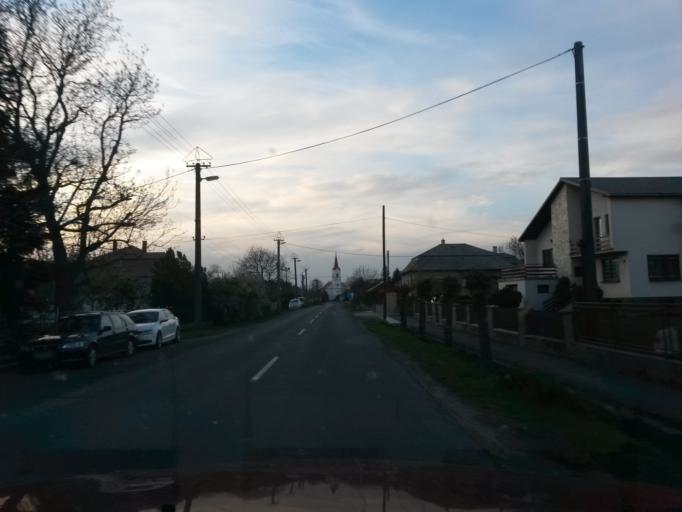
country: HU
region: Borsod-Abauj-Zemplen
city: Satoraljaujhely
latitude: 48.5102
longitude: 21.6204
